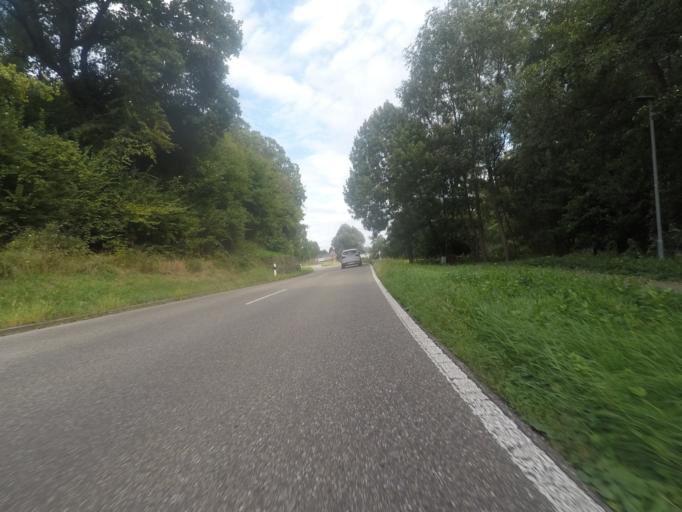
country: DE
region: Baden-Wuerttemberg
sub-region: Karlsruhe Region
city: Malsch
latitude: 48.8706
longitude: 8.3340
